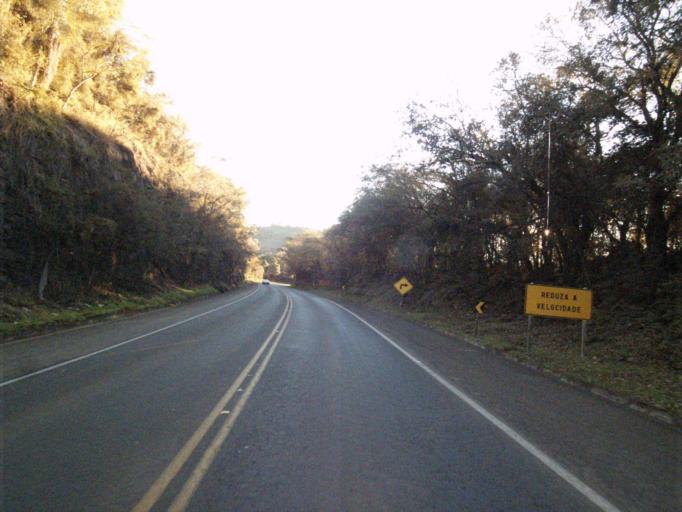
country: BR
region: Santa Catarina
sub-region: Chapeco
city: Chapeco
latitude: -26.8305
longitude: -53.0424
